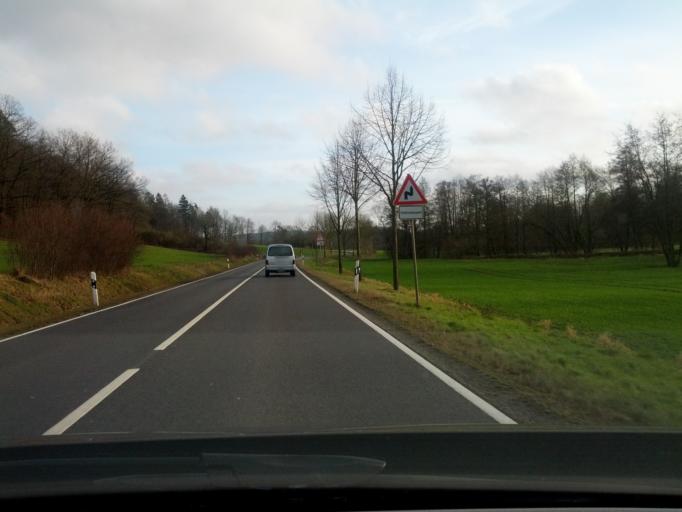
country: DE
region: Thuringia
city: Krauthausen
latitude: 51.0316
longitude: 10.2539
